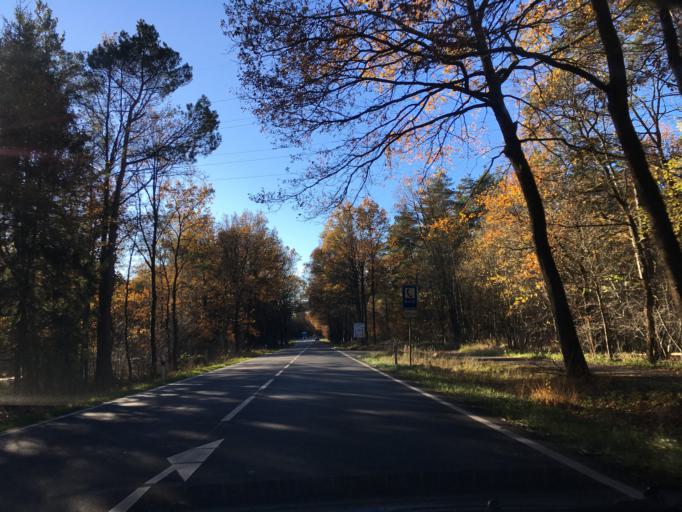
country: DE
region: Lower Saxony
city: Bispingen
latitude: 53.0586
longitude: 10.0314
